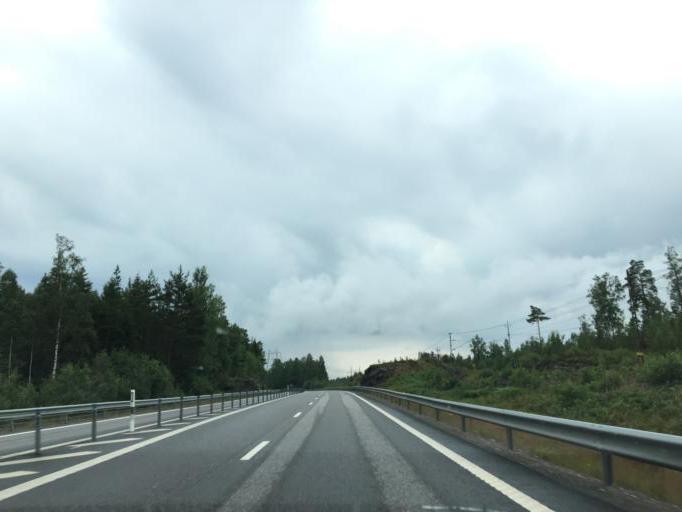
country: SE
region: OEstergoetland
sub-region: Norrkopings Kommun
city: Jursla
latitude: 58.8104
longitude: 16.1524
